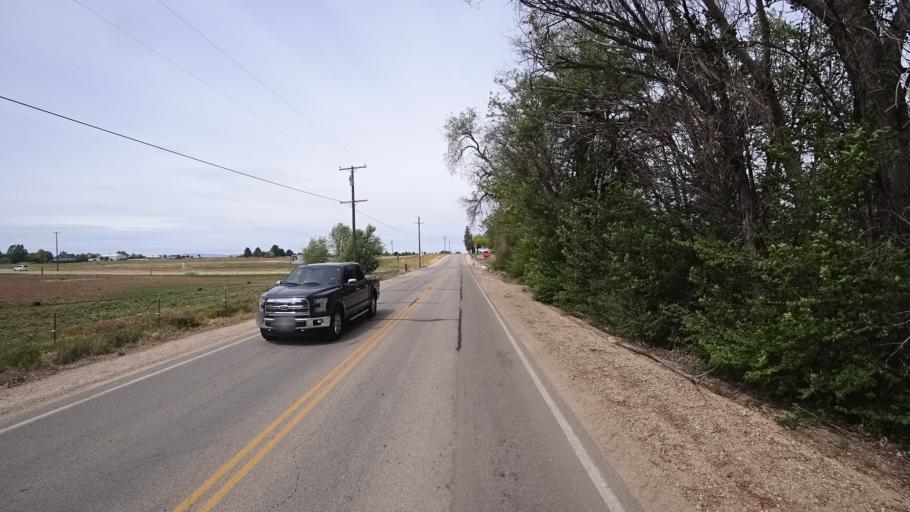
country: US
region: Idaho
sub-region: Ada County
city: Meridian
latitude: 43.5611
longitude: -116.4129
